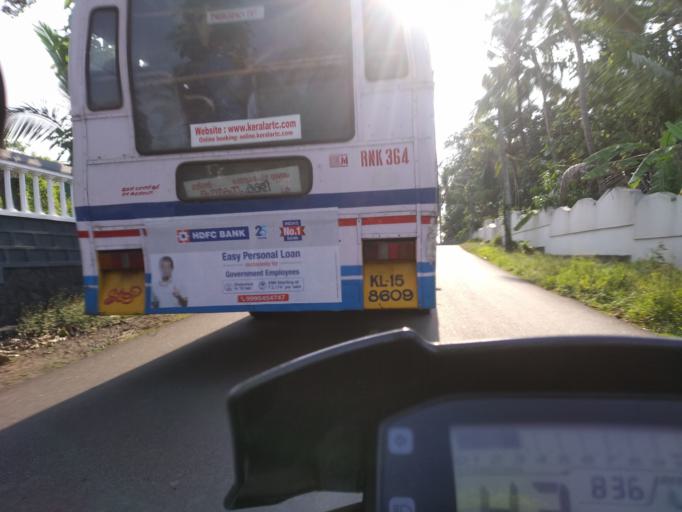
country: IN
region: Kerala
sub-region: Ernakulam
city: Ramamangalam
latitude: 9.9140
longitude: 76.4277
